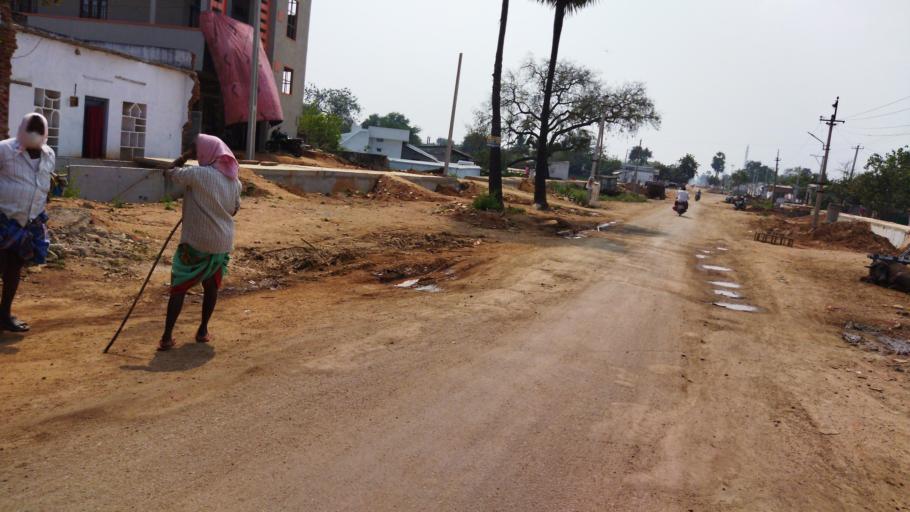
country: IN
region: Telangana
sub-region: Nalgonda
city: Nalgonda
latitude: 17.1252
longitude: 79.3681
